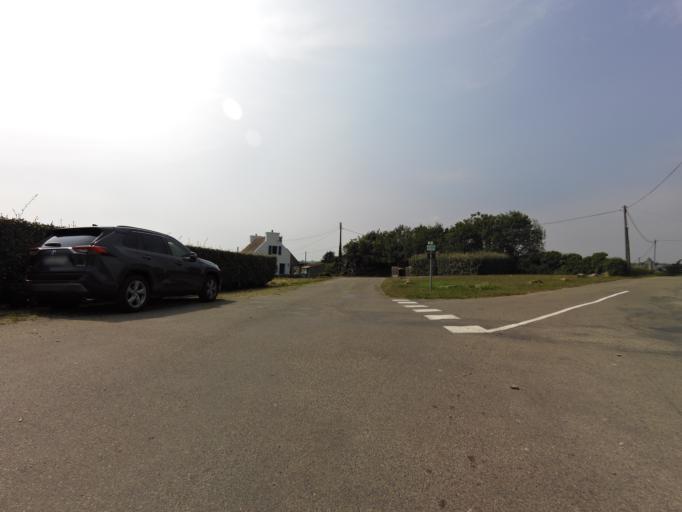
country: FR
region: Brittany
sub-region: Departement du Finistere
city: Esquibien
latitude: 48.0176
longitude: -4.5893
